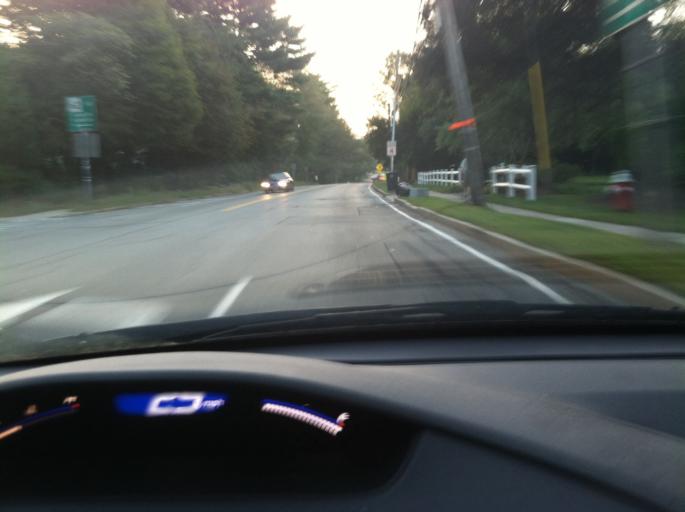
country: US
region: Massachusetts
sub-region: Middlesex County
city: Bedford
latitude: 42.4885
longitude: -71.2695
